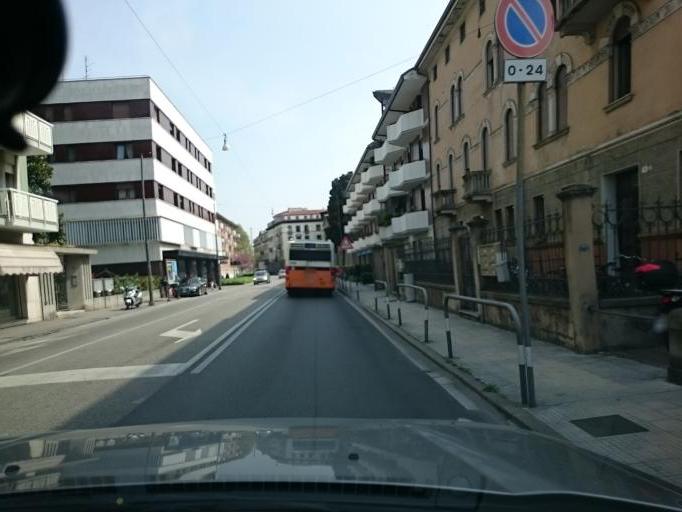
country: IT
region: Veneto
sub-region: Provincia di Padova
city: Padova
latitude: 45.3985
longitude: 11.8715
